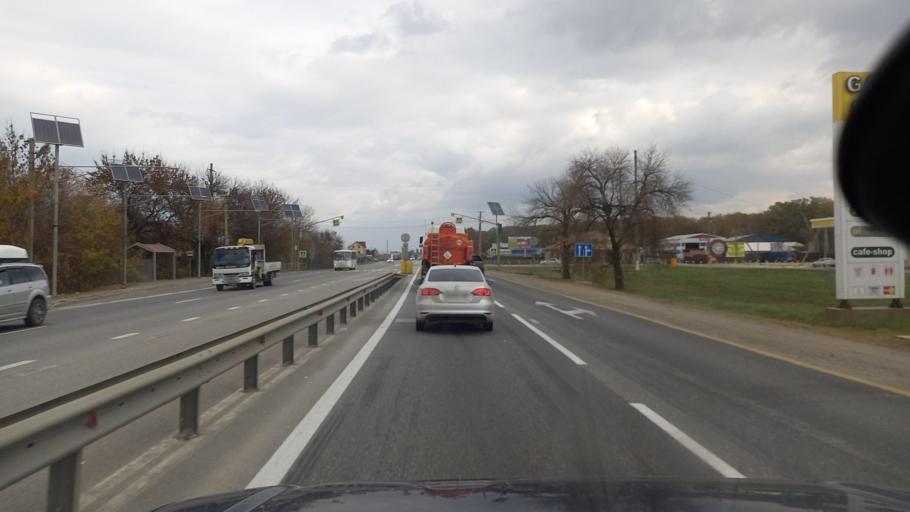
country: RU
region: Krasnodarskiy
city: Afipskiy
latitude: 44.9025
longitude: 38.8724
